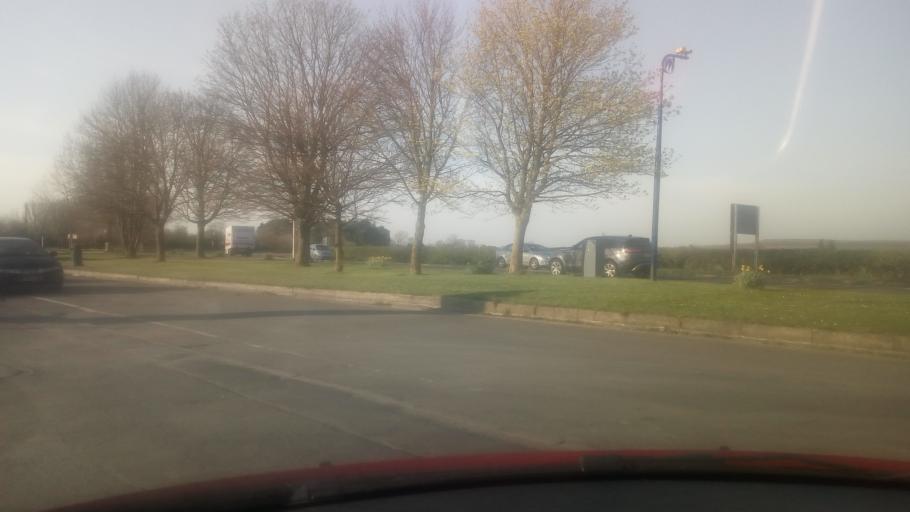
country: GB
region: England
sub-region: Nottinghamshire
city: Tuxford
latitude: 53.2576
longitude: -0.9260
